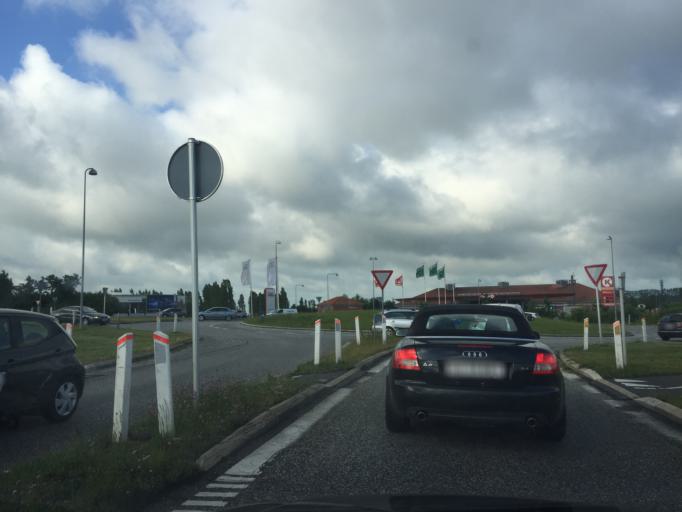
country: DK
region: Zealand
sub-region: Slagelse Kommune
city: Slagelse
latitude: 55.3886
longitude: 11.3642
